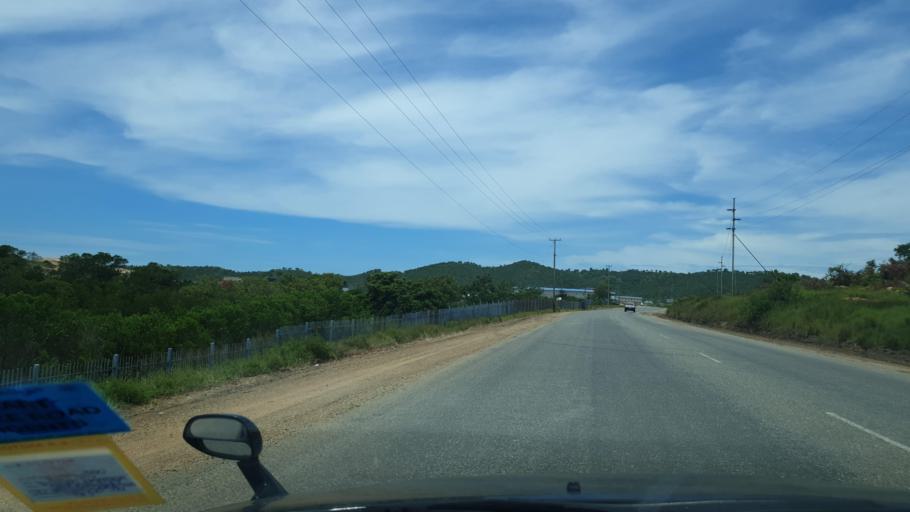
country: PG
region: National Capital
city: Port Moresby
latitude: -9.4192
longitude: 147.0871
